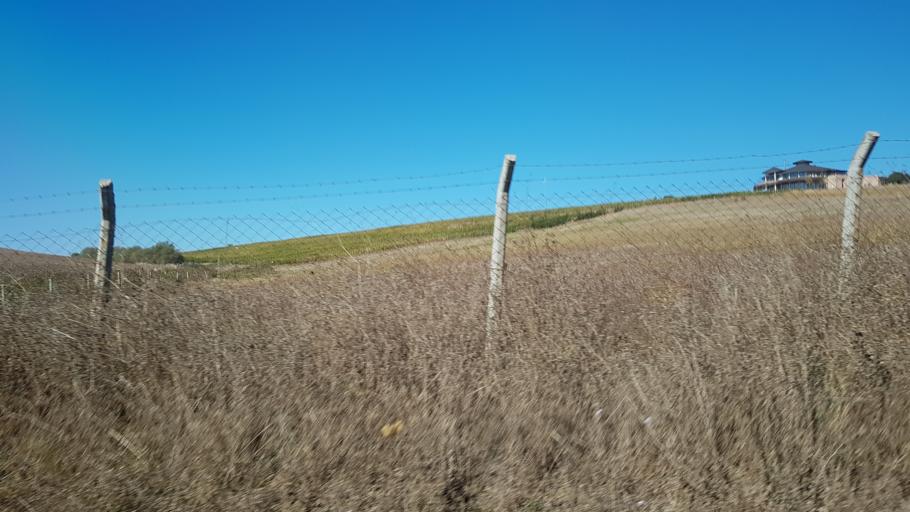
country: TR
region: Tekirdag
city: Corlu
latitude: 41.0376
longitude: 27.8143
